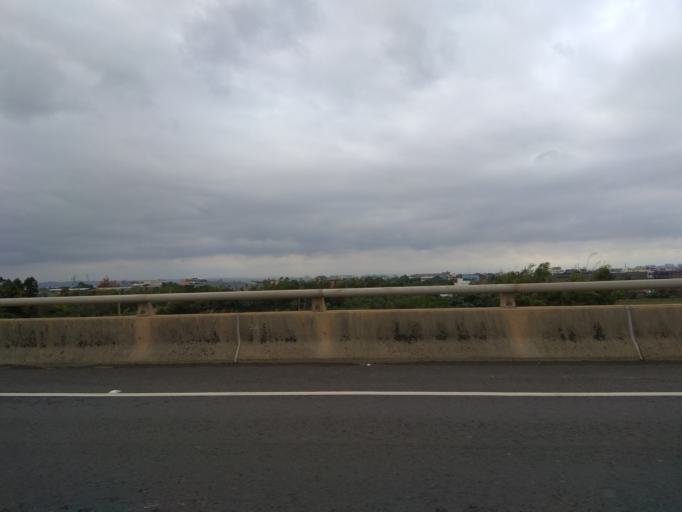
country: TW
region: Taiwan
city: Taoyuan City
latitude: 25.0918
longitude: 121.1924
